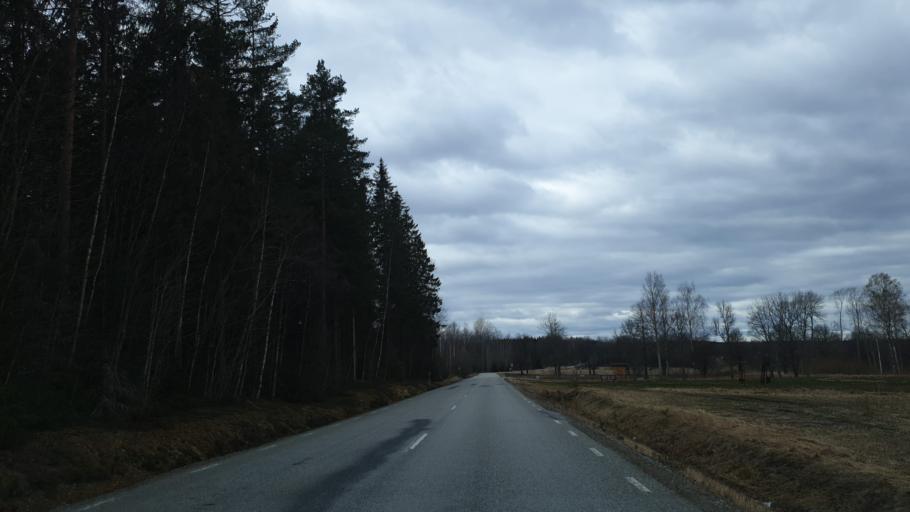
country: SE
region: OErebro
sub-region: Nora Kommun
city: As
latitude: 59.5814
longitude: 14.9733
